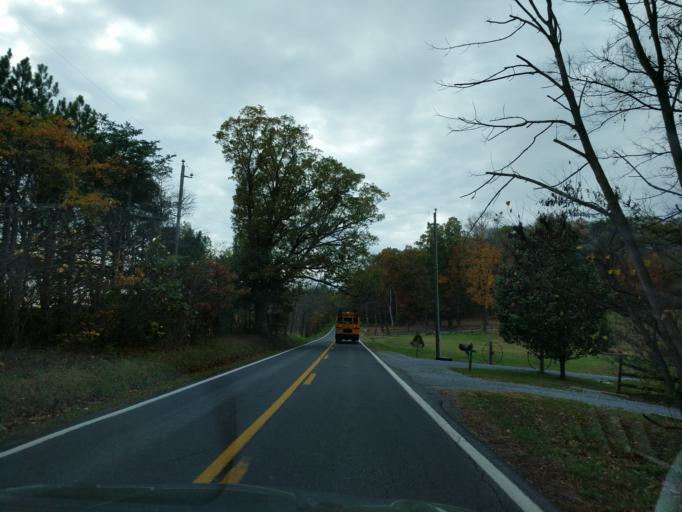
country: US
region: West Virginia
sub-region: Berkeley County
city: Inwood
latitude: 39.3930
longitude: -78.1815
